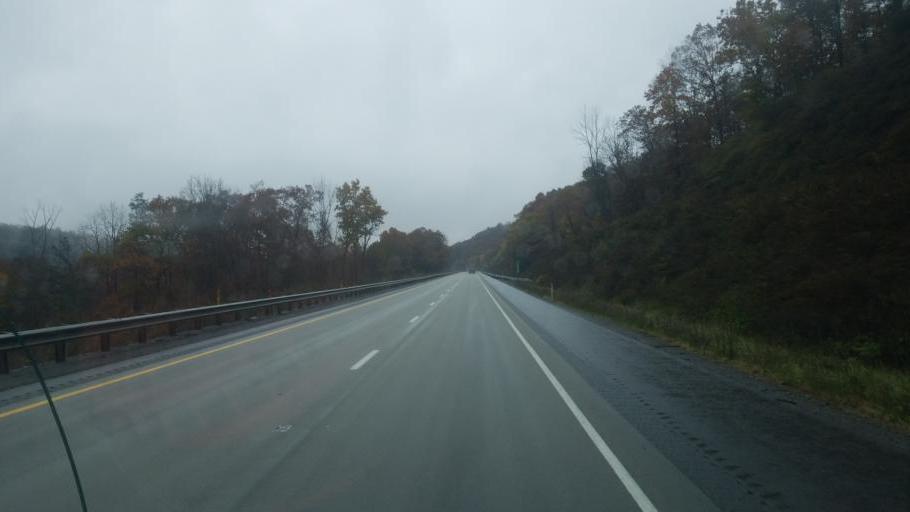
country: US
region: Pennsylvania
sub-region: Centre County
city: Milesburg
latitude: 40.9734
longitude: -77.7936
